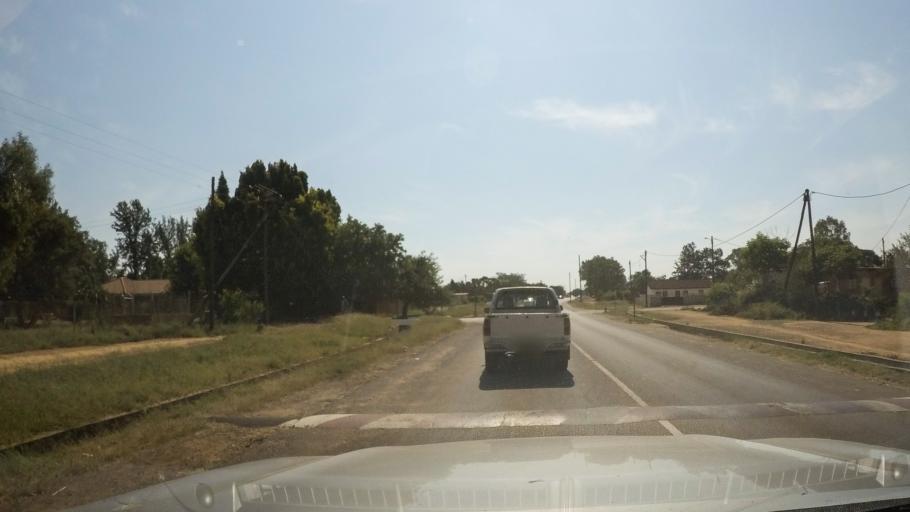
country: BW
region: South East
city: Lobatse
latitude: -25.2106
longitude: 25.6829
